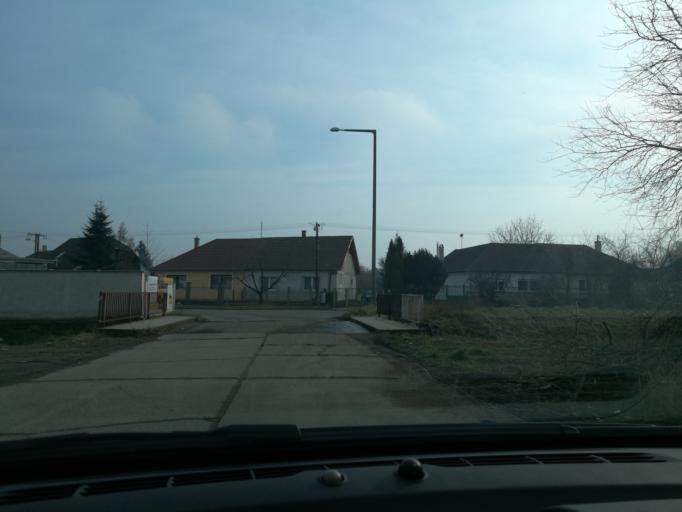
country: HU
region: Szabolcs-Szatmar-Bereg
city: Nyiregyhaza
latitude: 47.9607
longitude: 21.6985
